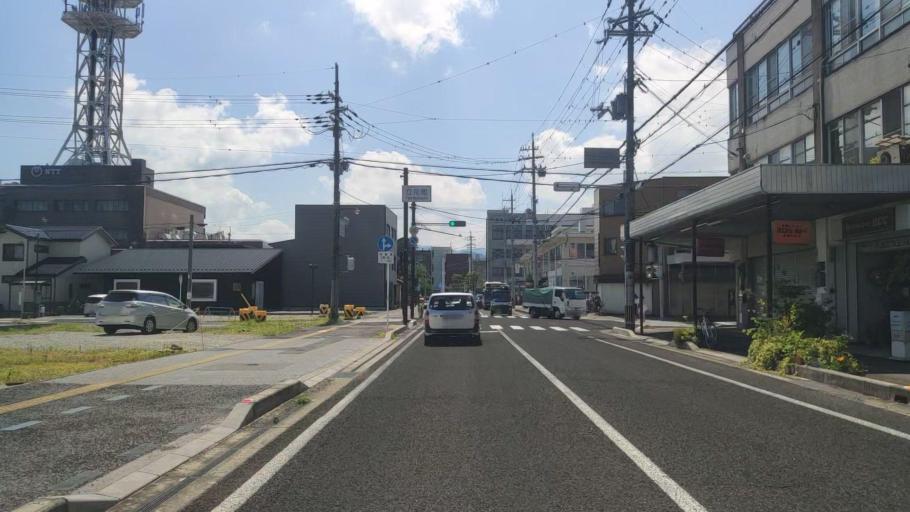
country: JP
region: Shiga Prefecture
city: Hikone
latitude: 35.2711
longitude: 136.2550
